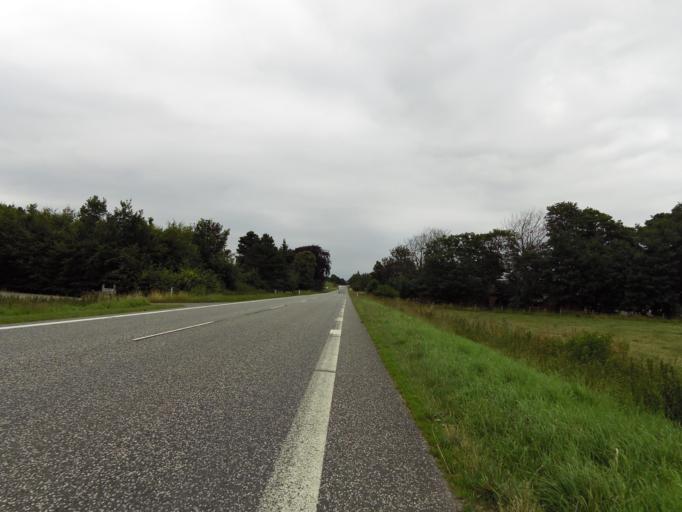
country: DK
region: South Denmark
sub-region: Tonder Kommune
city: Logumkloster
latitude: 55.1152
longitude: 8.9548
